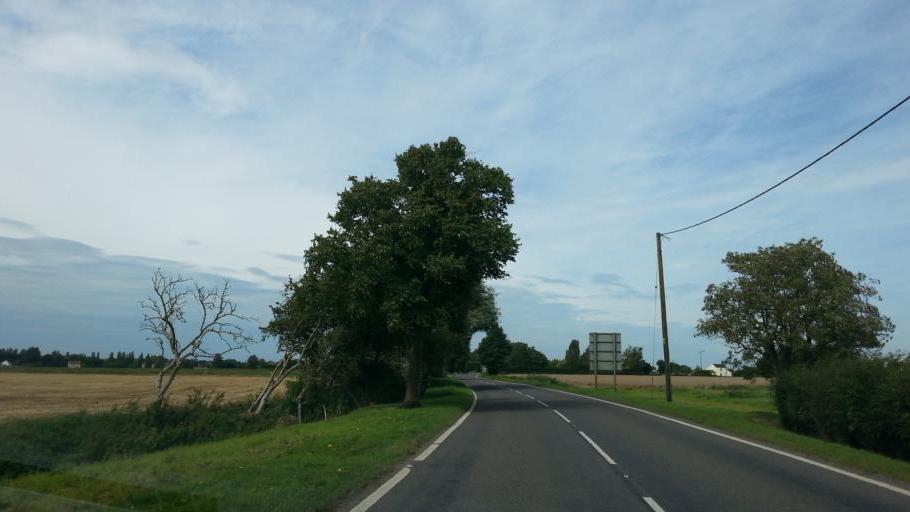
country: GB
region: England
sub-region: Norfolk
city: Outwell
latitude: 52.5664
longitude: 0.2291
